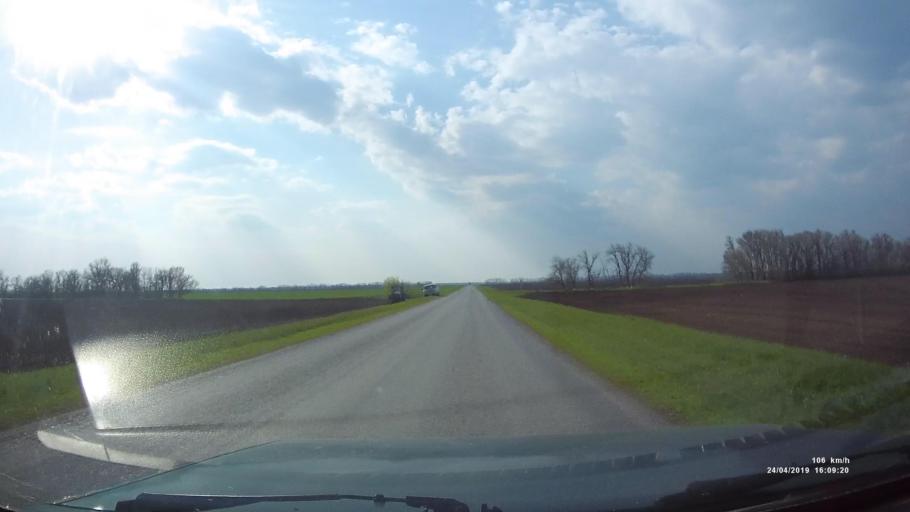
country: RU
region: Rostov
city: Sovetskoye
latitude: 46.7071
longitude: 42.2918
